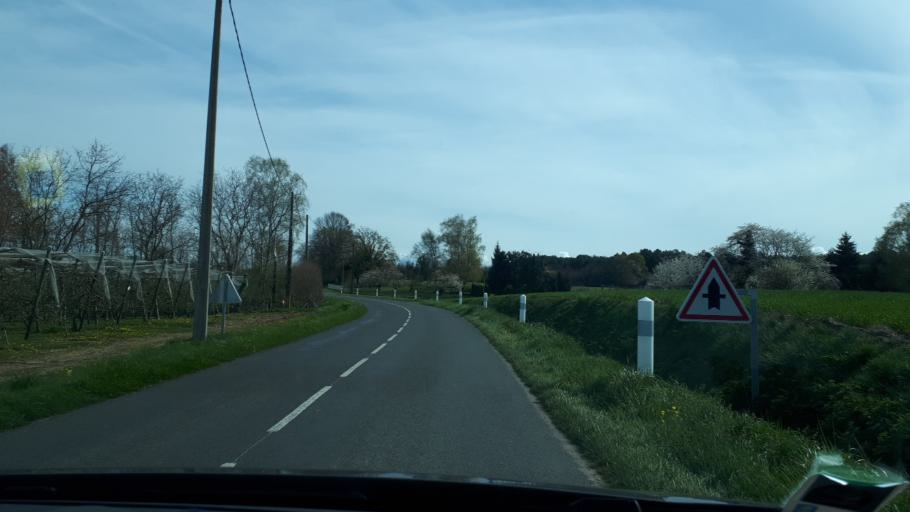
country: FR
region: Pays de la Loire
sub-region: Departement de la Sarthe
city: Yvre-le-Polin
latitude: 47.8122
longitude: 0.1225
